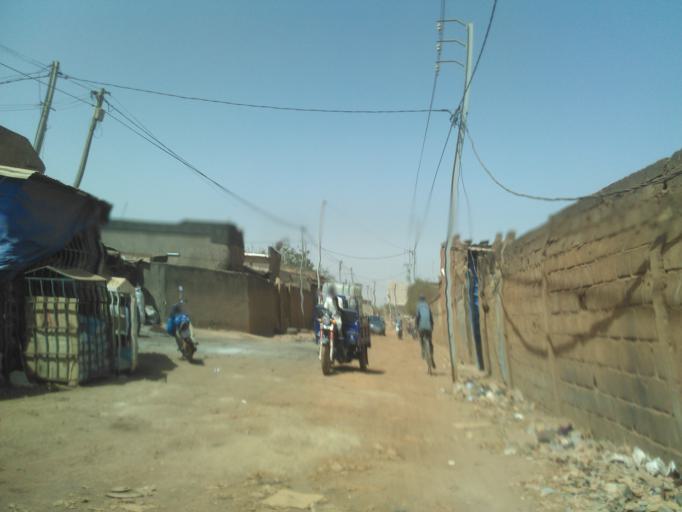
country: BF
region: Centre
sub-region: Kadiogo Province
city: Ouagadougou
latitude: 12.3865
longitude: -1.5629
